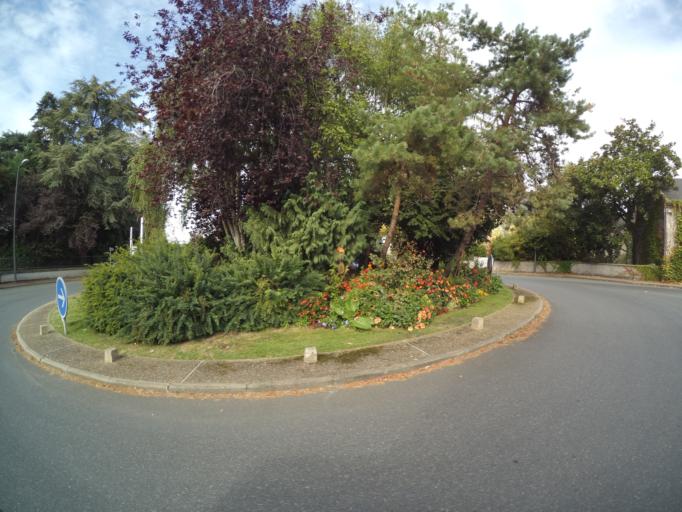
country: FR
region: Pays de la Loire
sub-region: Departement de Maine-et-Loire
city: Doue-la-Fontaine
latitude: 47.1974
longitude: -0.2748
